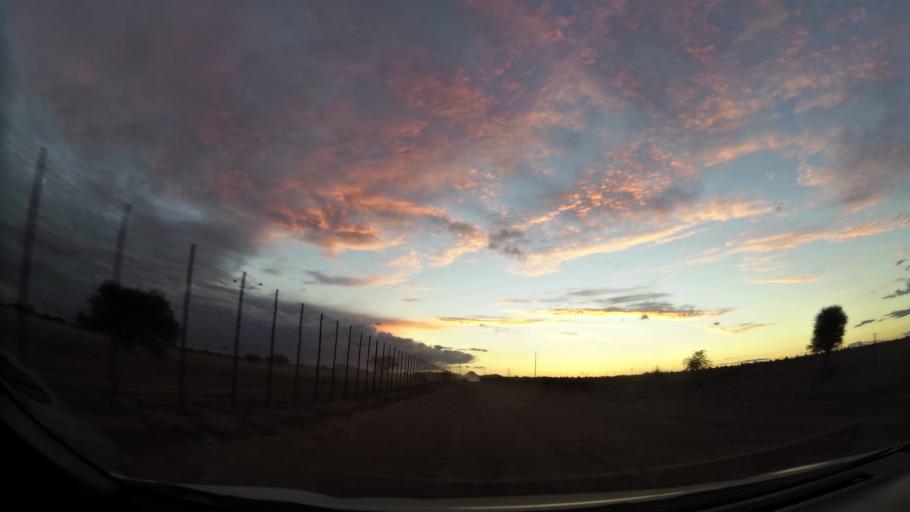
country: ZA
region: Limpopo
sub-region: Capricorn District Municipality
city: Polokwane
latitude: -23.7329
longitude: 29.4107
